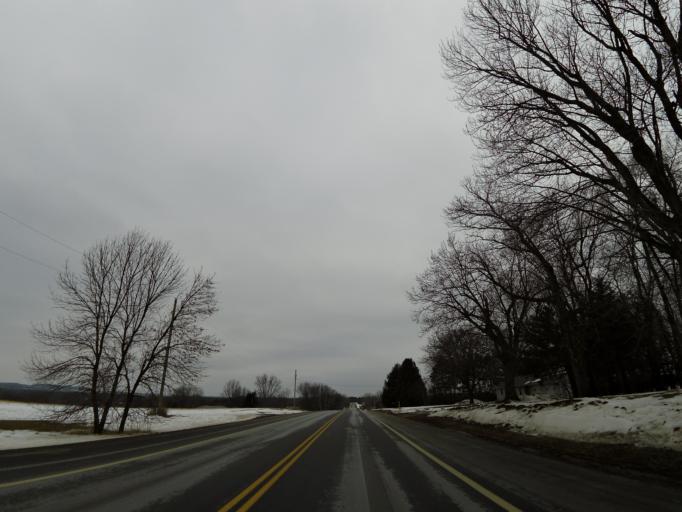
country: US
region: Wisconsin
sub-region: Pierce County
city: Prescott
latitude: 44.8247
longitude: -92.8000
